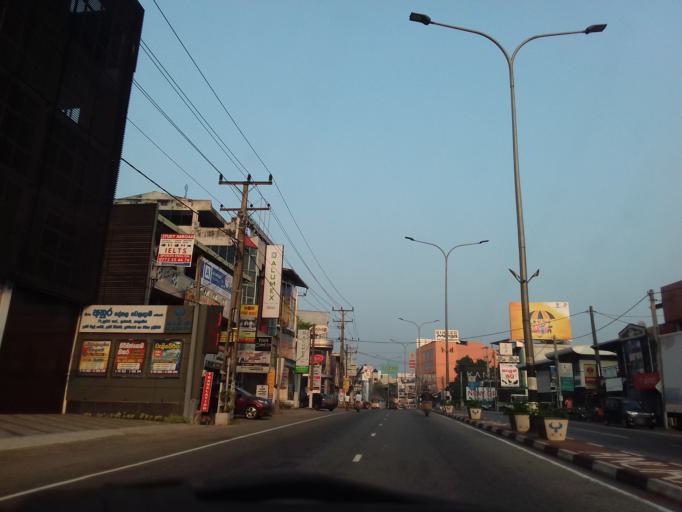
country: LK
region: Western
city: Kelaniya
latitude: 6.9735
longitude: 79.9203
